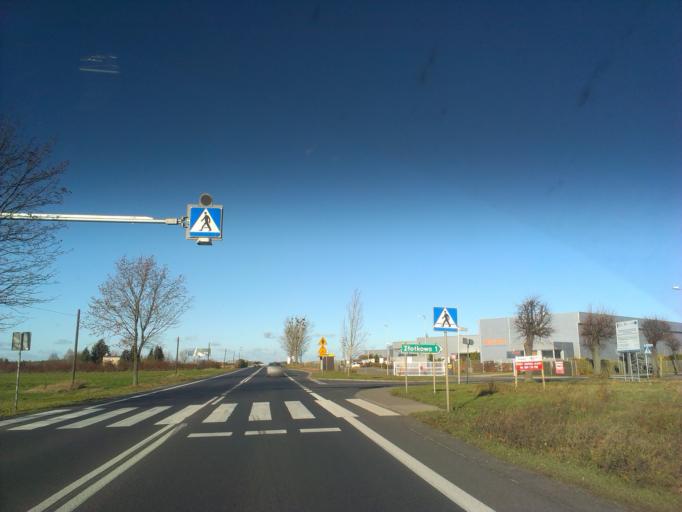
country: PL
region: Greater Poland Voivodeship
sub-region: Powiat poznanski
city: Zlotniki
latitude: 52.5073
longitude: 16.8351
